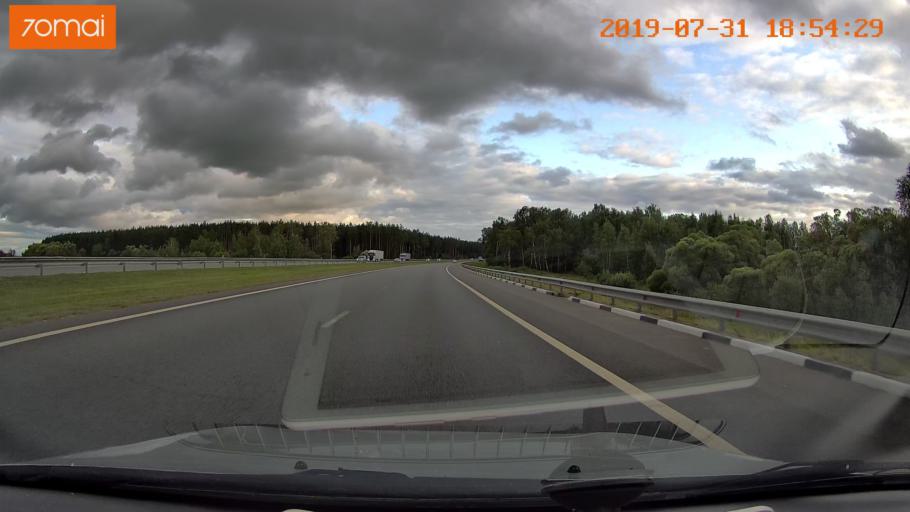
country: RU
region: Moskovskaya
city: Raduzhnyy
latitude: 55.1893
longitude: 38.6684
